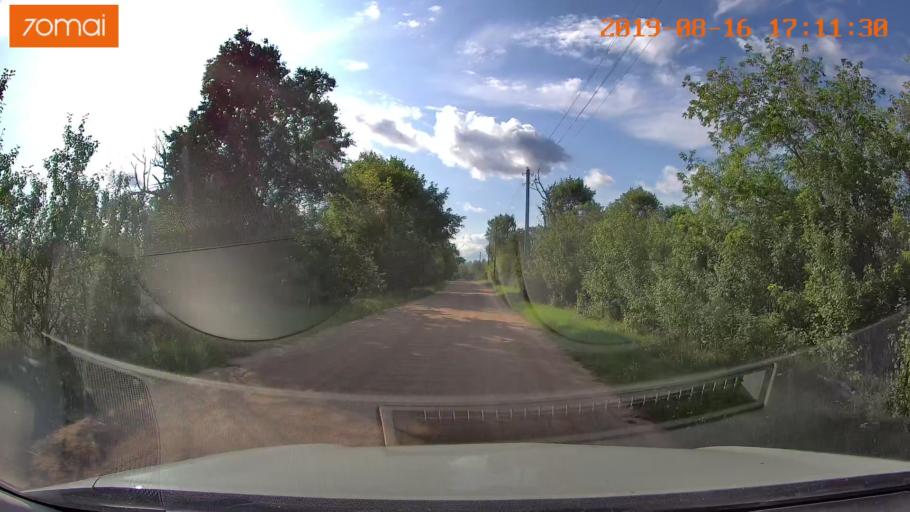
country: BY
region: Mogilev
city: Hlusha
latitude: 53.1958
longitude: 28.9051
